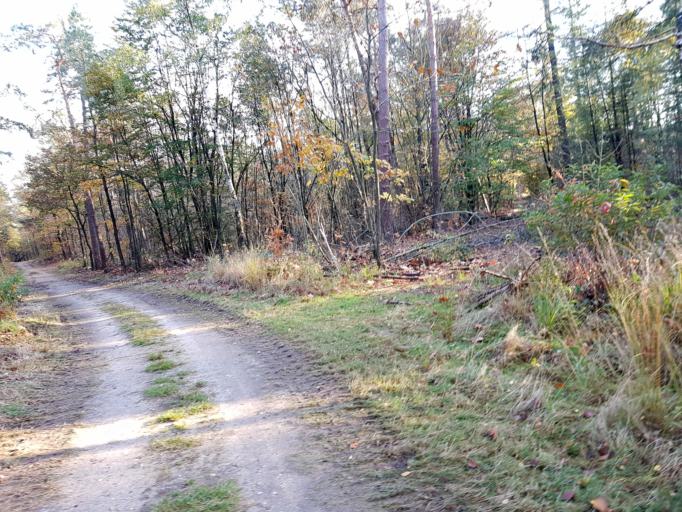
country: NL
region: Gelderland
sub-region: Gemeente Groesbeek
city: Groesbeek
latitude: 51.7882
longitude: 5.9083
